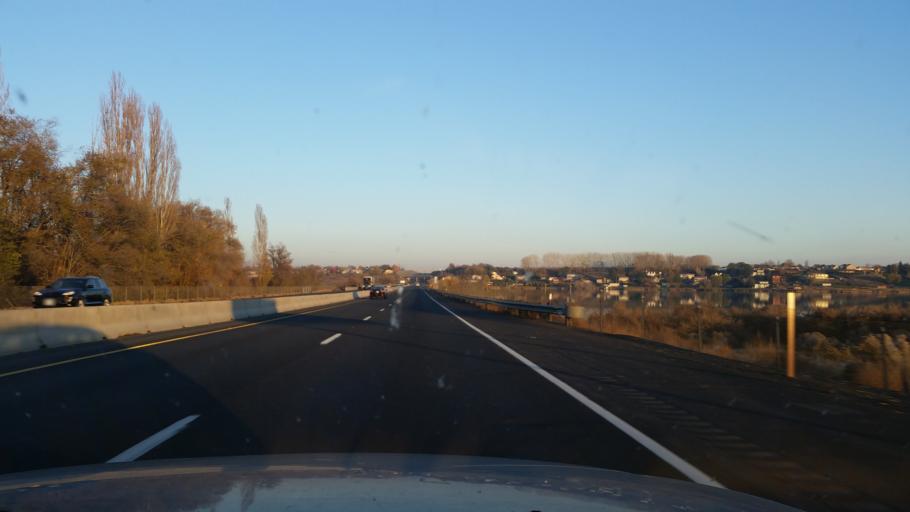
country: US
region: Washington
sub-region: Grant County
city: Moses Lake
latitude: 47.1010
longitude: -119.3033
